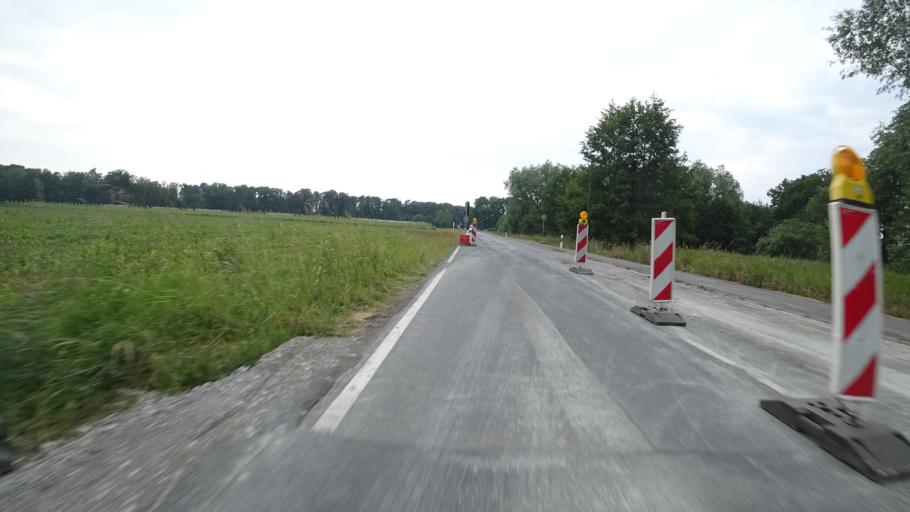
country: DE
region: North Rhine-Westphalia
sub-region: Regierungsbezirk Detmold
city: Guetersloh
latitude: 51.9223
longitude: 8.3726
